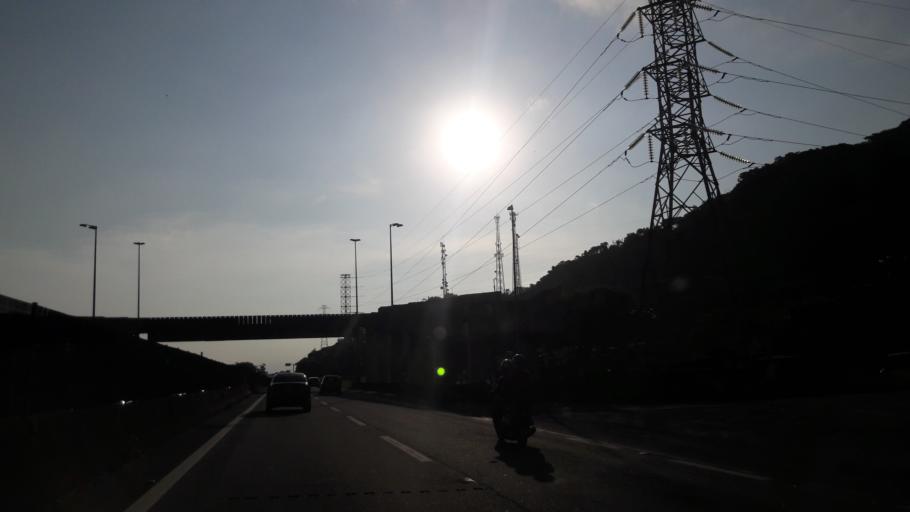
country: BR
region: Sao Paulo
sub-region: Mongagua
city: Mongagua
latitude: -24.0969
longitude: -46.6285
